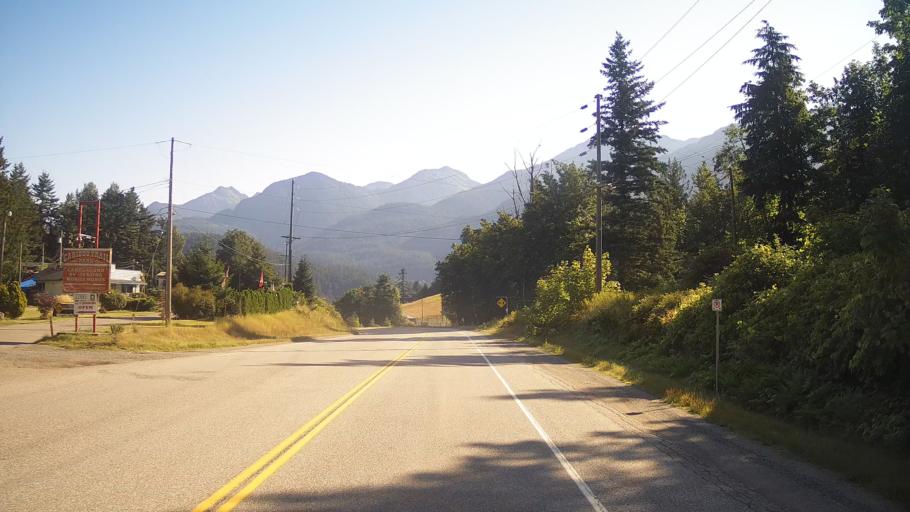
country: CA
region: British Columbia
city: Hope
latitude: 49.4135
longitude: -121.4399
